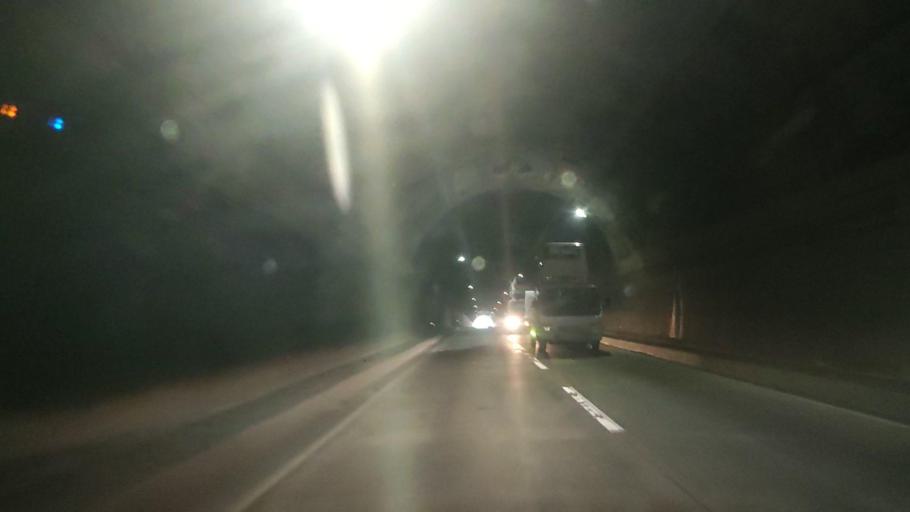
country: JP
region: Kagoshima
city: Okuchi-shinohara
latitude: 31.9749
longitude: 130.7412
